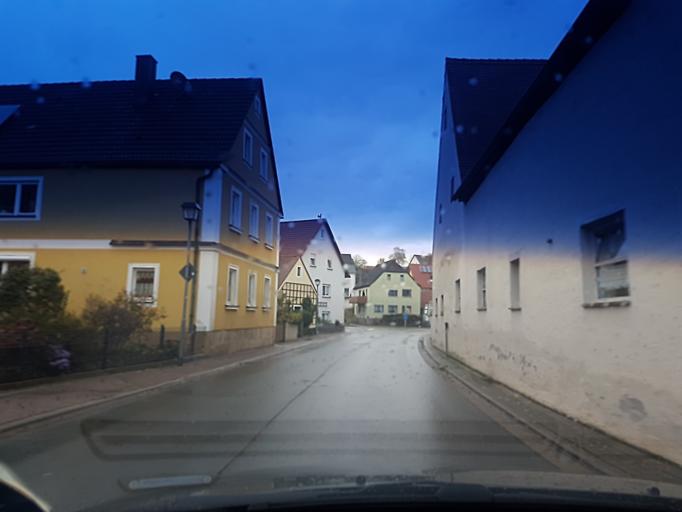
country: DE
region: Bavaria
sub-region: Upper Franconia
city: Pommersfelden
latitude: 49.7725
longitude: 10.8039
